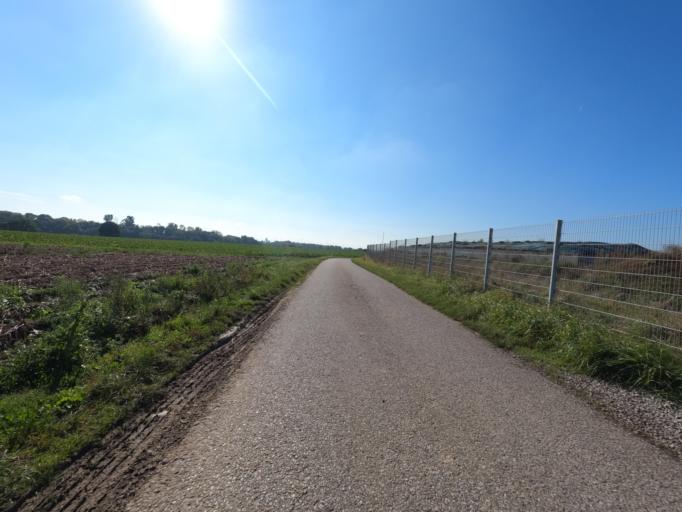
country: DE
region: North Rhine-Westphalia
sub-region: Regierungsbezirk Koln
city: Linnich
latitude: 51.0001
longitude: 6.2995
